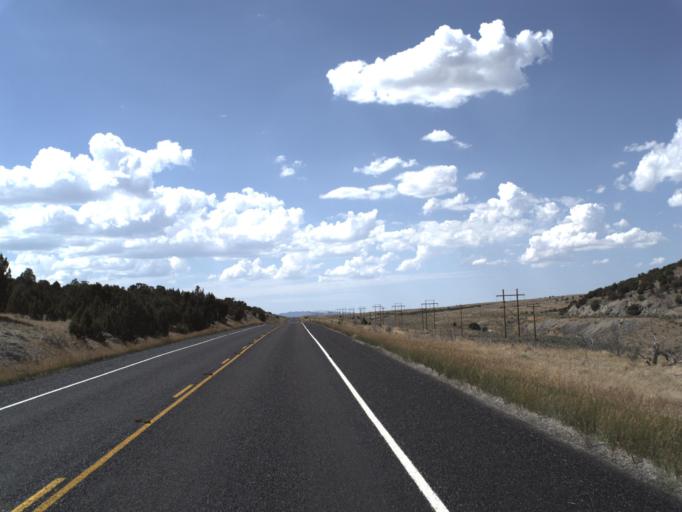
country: US
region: Idaho
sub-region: Minidoka County
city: Rupert
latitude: 41.9753
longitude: -113.1588
